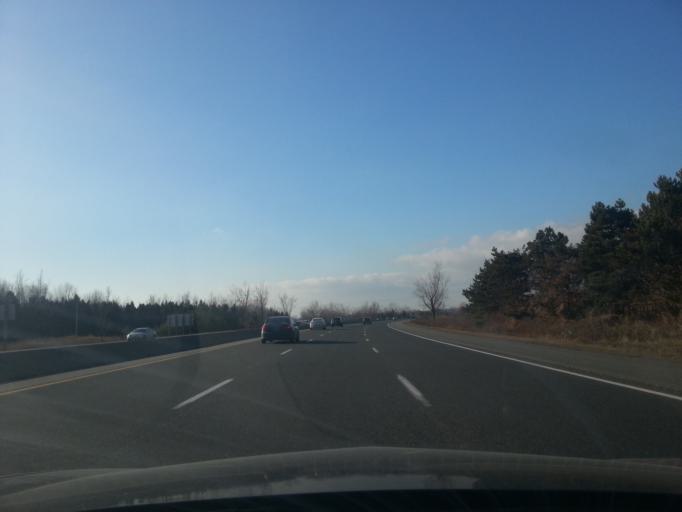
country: CA
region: Ontario
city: Oshawa
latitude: 43.8757
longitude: -78.7888
